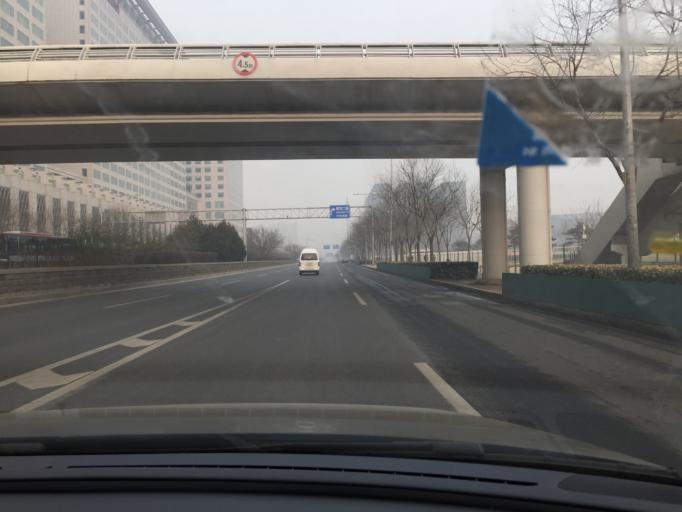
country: CN
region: Beijing
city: Datun
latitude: 39.9895
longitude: 116.3812
